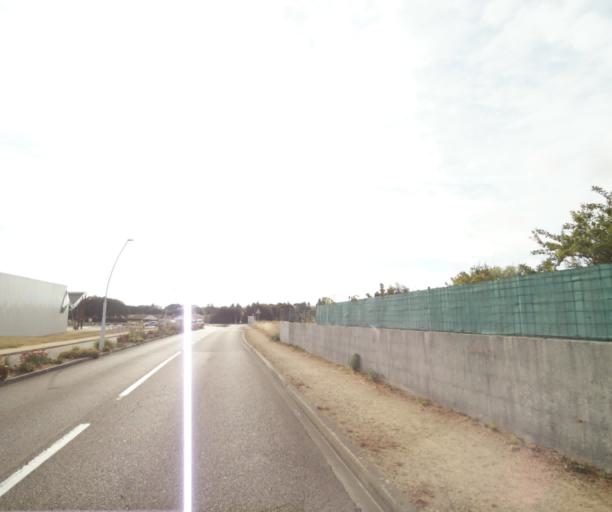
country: FR
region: Pays de la Loire
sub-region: Departement de la Vendee
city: Chateau-d'Olonne
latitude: 46.5030
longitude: -1.7353
